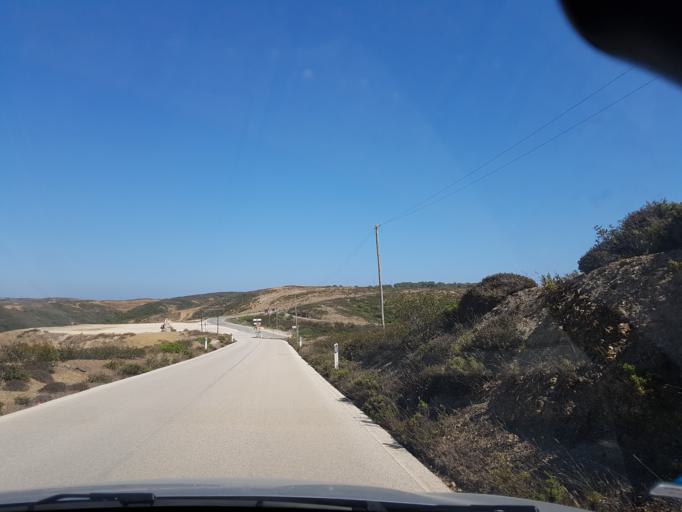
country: PT
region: Faro
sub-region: Vila do Bispo
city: Vila do Bispo
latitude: 37.0966
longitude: -8.9358
